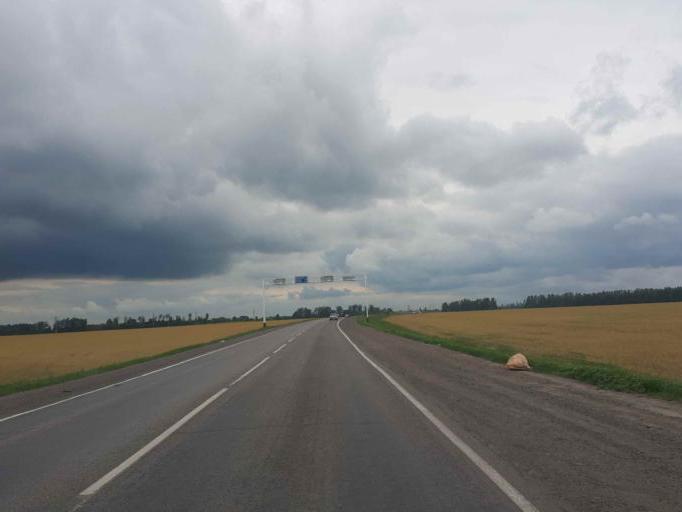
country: RU
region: Tambov
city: Komsomolets
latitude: 52.7383
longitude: 41.2943
